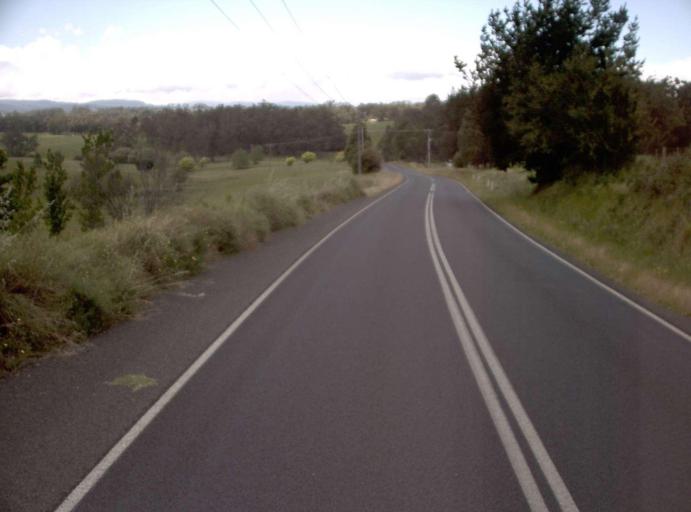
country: AU
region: Victoria
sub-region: Baw Baw
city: Warragul
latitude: -38.0890
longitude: 145.9200
